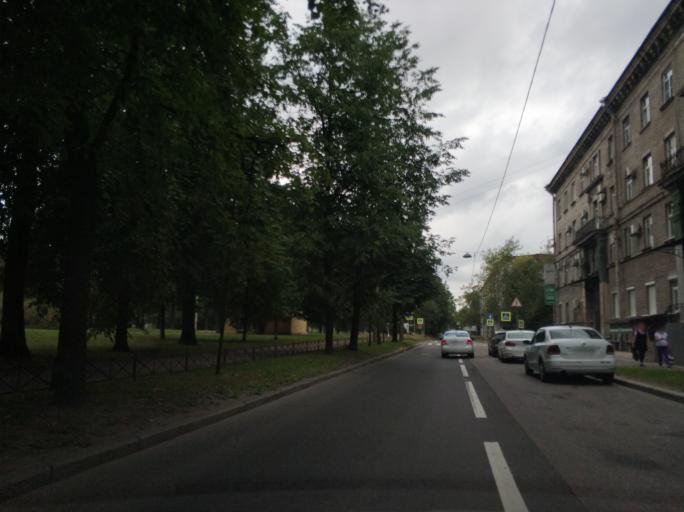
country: RU
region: St.-Petersburg
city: Novaya Derevnya
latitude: 59.9860
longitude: 30.2871
